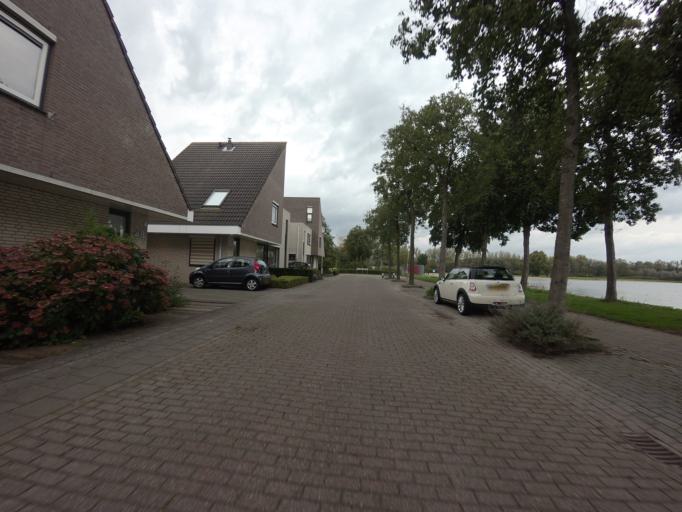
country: NL
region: North Brabant
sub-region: Gemeente Breda
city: Hoge Vucht
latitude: 51.6257
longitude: 4.7503
